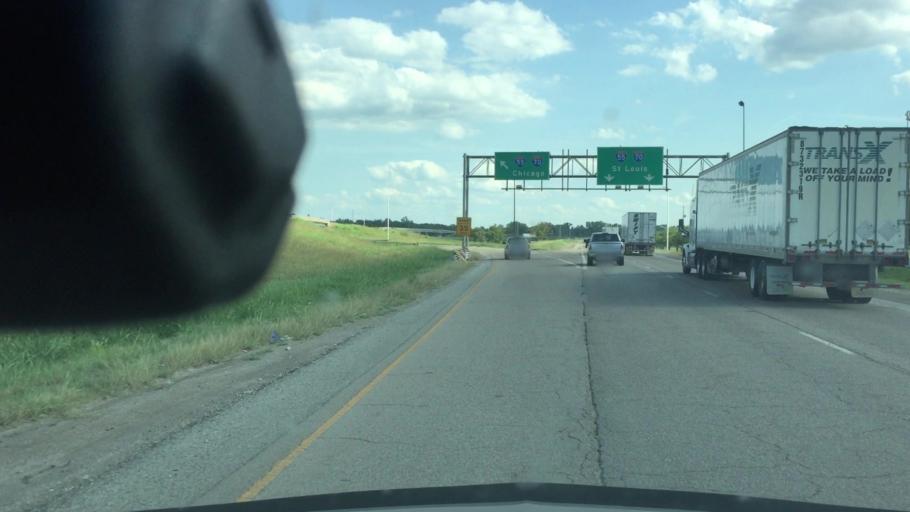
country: US
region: Illinois
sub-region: Saint Clair County
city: East Saint Louis
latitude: 38.6500
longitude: -90.1328
